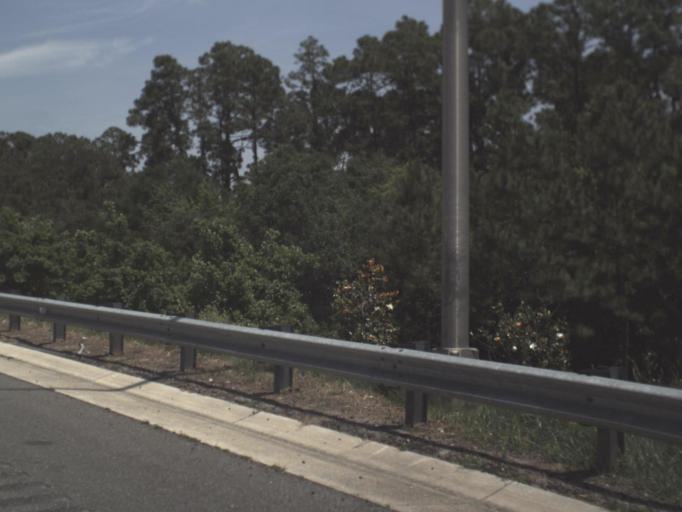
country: US
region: Florida
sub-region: Duval County
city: Neptune Beach
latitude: 30.3078
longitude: -81.5236
